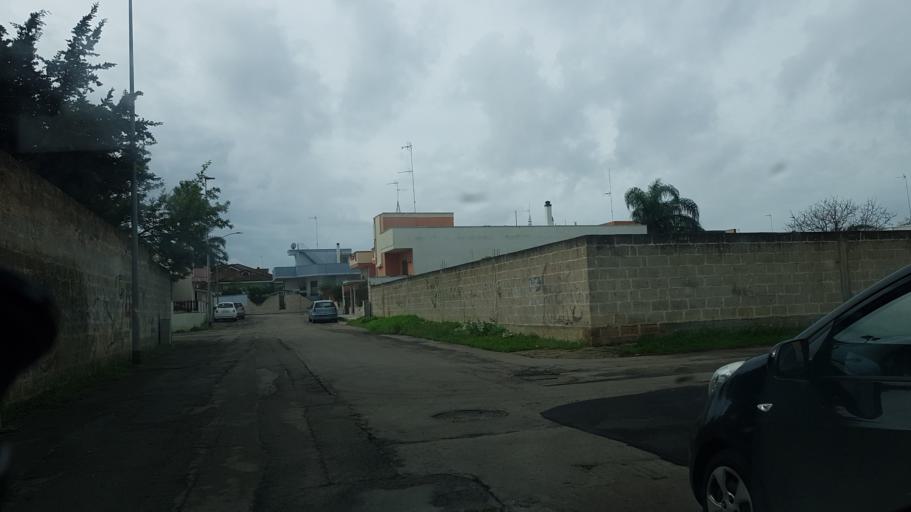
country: IT
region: Apulia
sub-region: Provincia di Lecce
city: Carmiano
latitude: 40.3437
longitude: 18.0521
